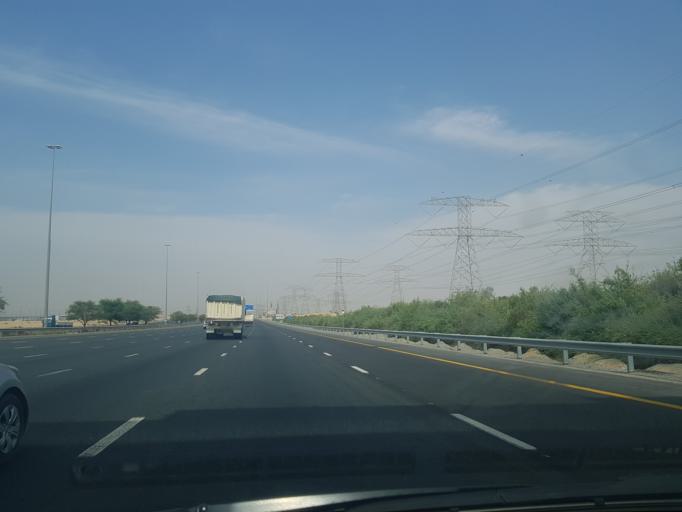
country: AE
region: Ash Shariqah
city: Sharjah
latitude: 25.2153
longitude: 55.5555
